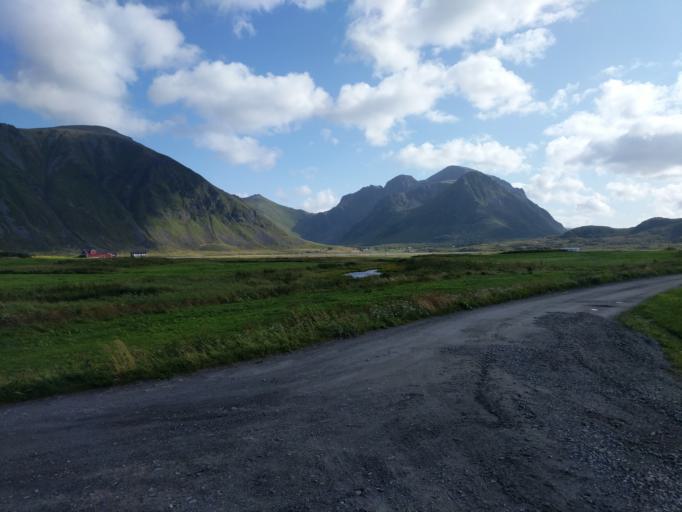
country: NO
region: Nordland
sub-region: Vestvagoy
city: Evjen
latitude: 68.3368
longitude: 13.8863
